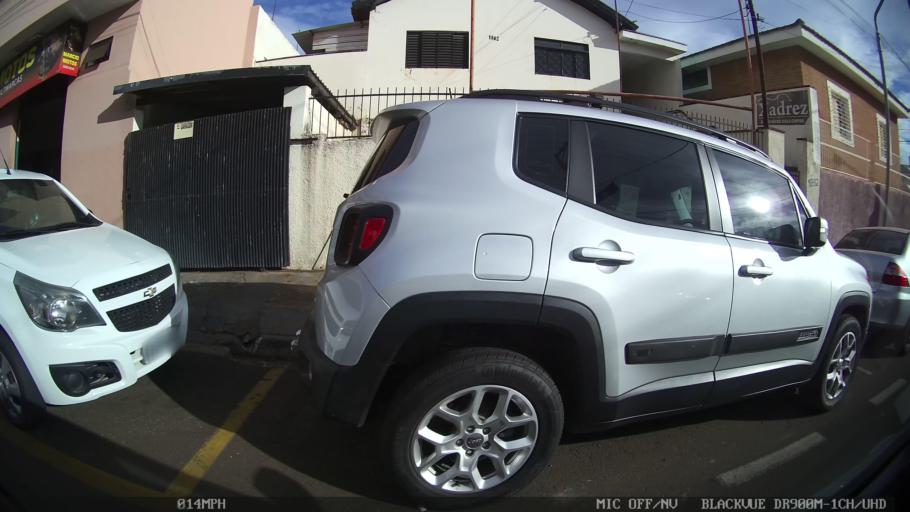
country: BR
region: Sao Paulo
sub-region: Catanduva
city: Catanduva
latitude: -21.1464
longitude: -48.9766
